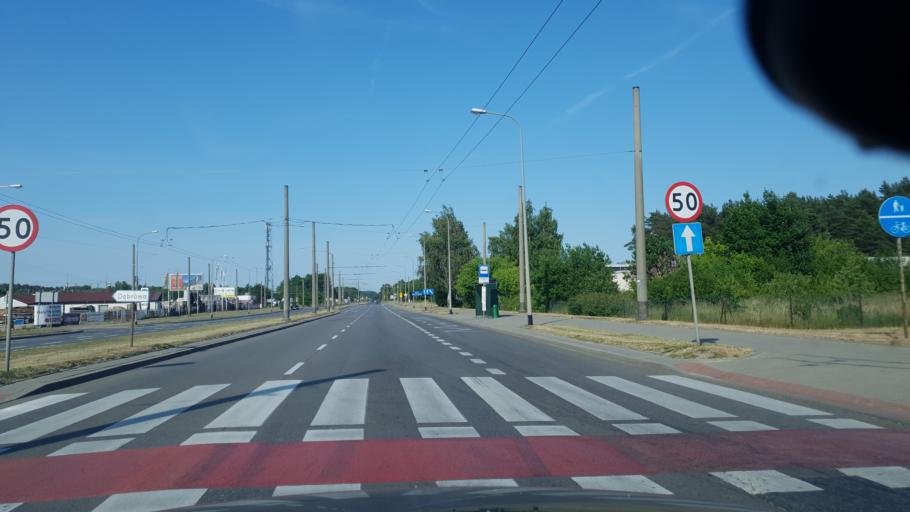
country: PL
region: Pomeranian Voivodeship
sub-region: Powiat kartuski
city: Chwaszczyno
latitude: 54.4573
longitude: 18.4505
